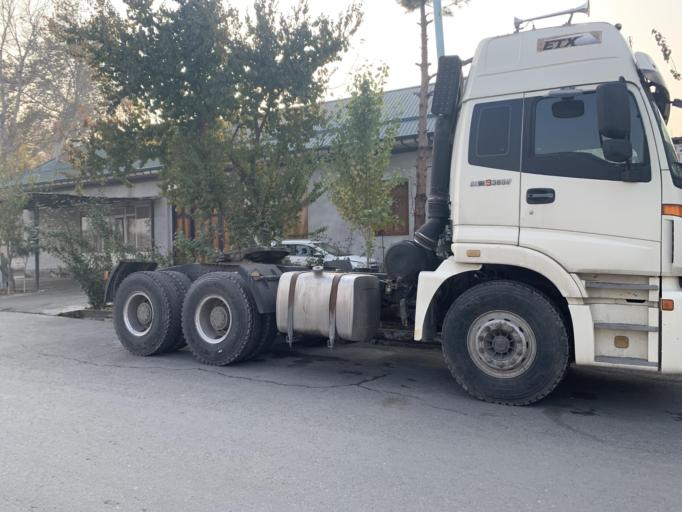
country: UZ
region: Fergana
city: Qo`qon
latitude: 40.5392
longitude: 70.9352
